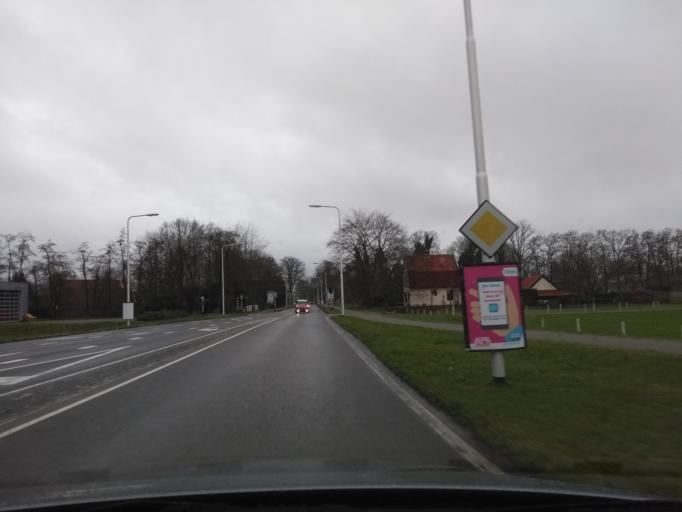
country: NL
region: Overijssel
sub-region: Gemeente Almelo
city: Almelo
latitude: 52.3782
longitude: 6.6647
